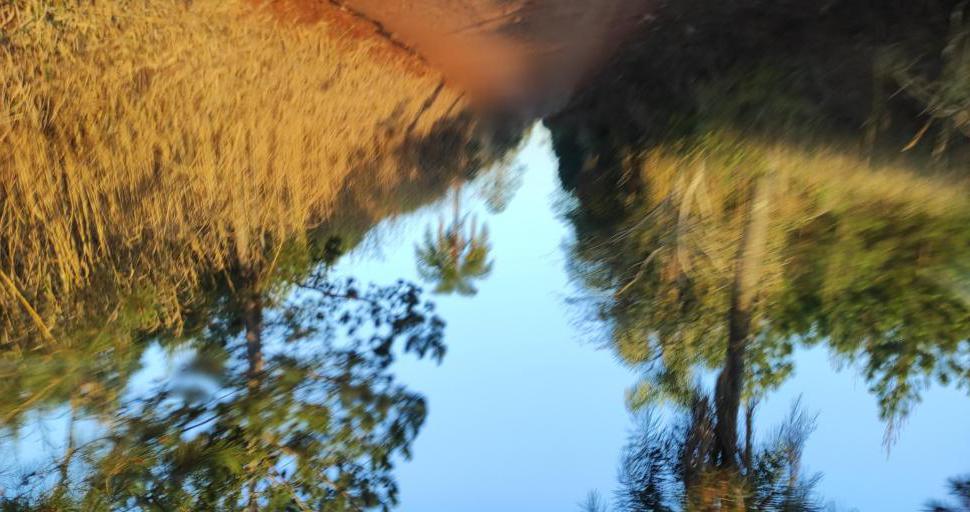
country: AR
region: Misiones
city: Capiovi
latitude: -26.8808
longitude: -55.1129
